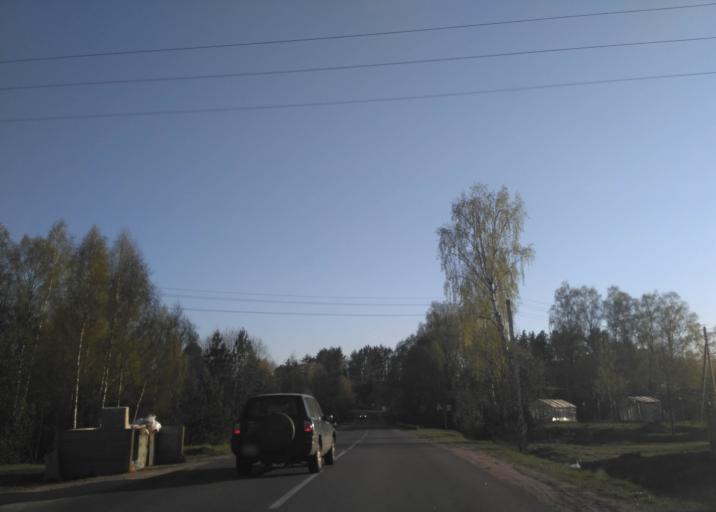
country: BY
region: Minsk
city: Pyatryshki
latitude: 54.1185
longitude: 27.1950
